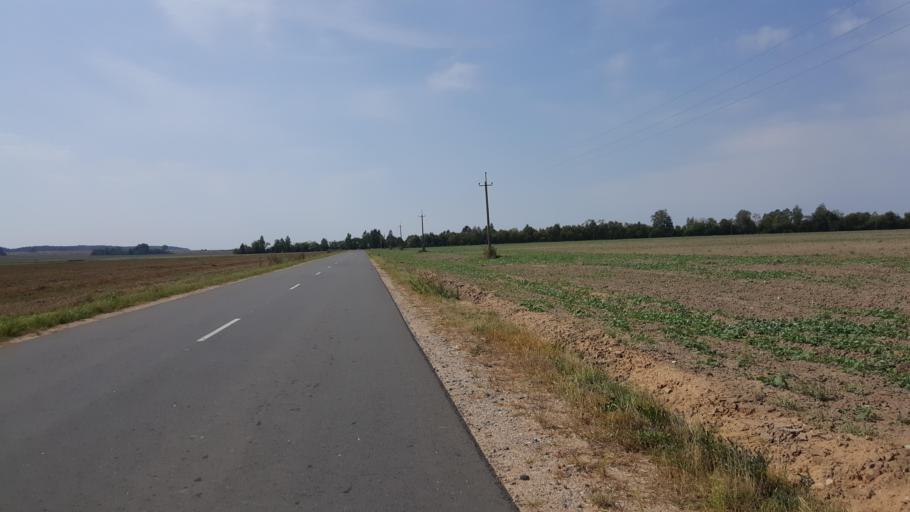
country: BY
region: Brest
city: Kamyanyets
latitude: 52.4728
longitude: 23.7153
